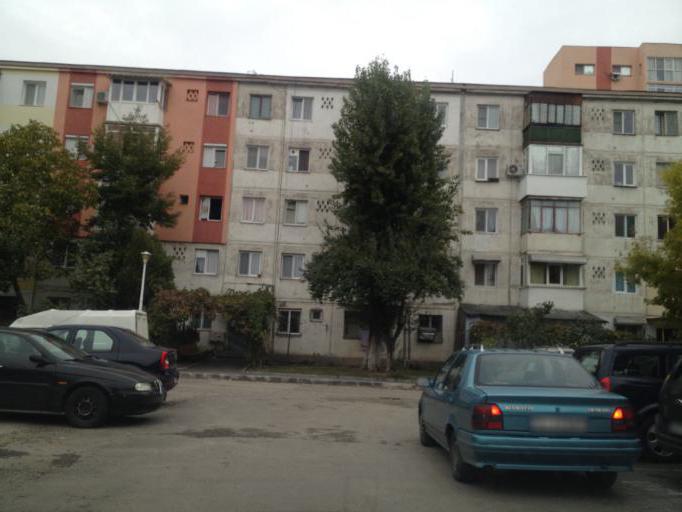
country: RO
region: Dolj
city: Craiova
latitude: 44.3338
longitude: 23.7825
